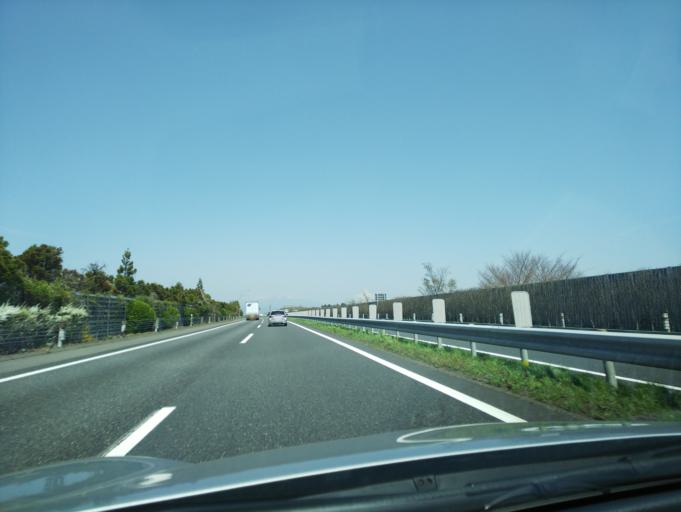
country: JP
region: Fukushima
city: Koriyama
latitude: 37.3842
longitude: 140.3127
